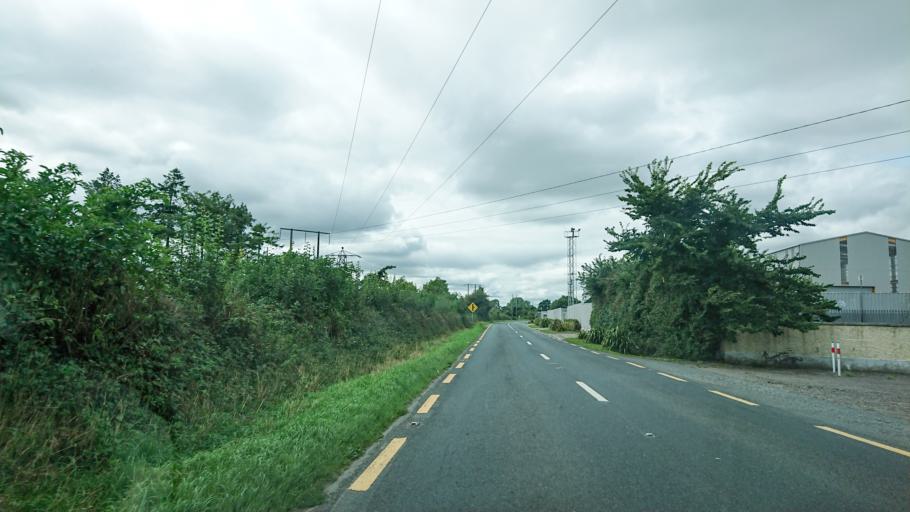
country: IE
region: Munster
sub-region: Waterford
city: Dungarvan
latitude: 52.1076
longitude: -7.6545
